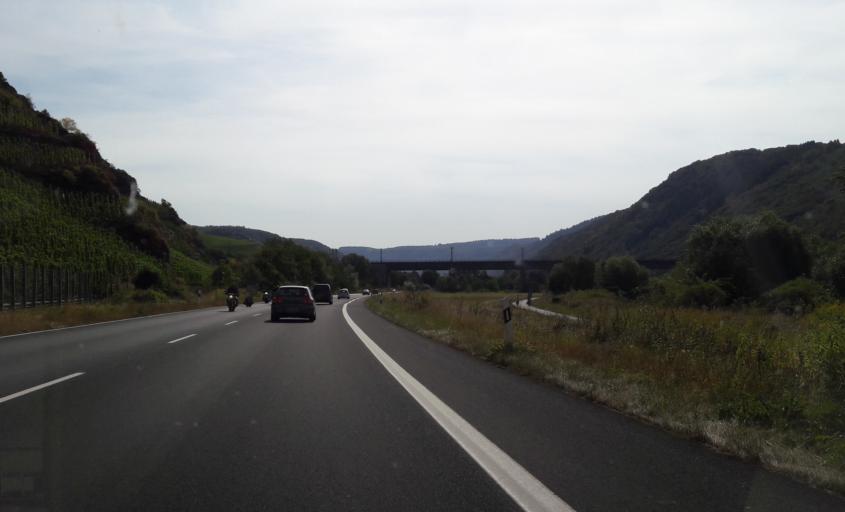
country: DE
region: Rheinland-Pfalz
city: Neef
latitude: 50.1048
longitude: 7.1325
